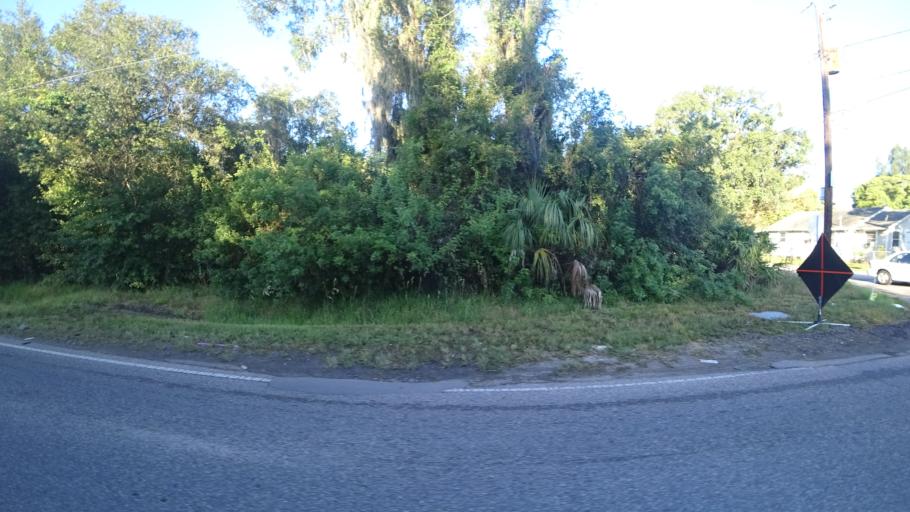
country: US
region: Florida
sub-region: Manatee County
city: Ellenton
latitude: 27.5467
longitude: -82.5282
